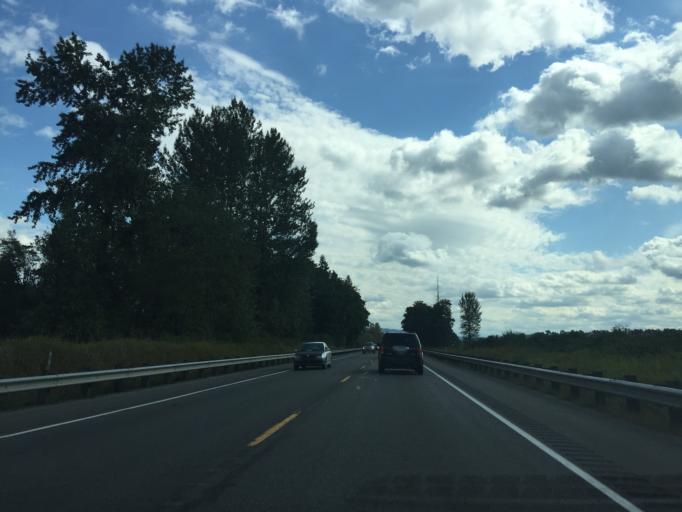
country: US
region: Washington
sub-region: Snohomish County
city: Three Lakes
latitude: 47.8937
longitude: -122.0308
